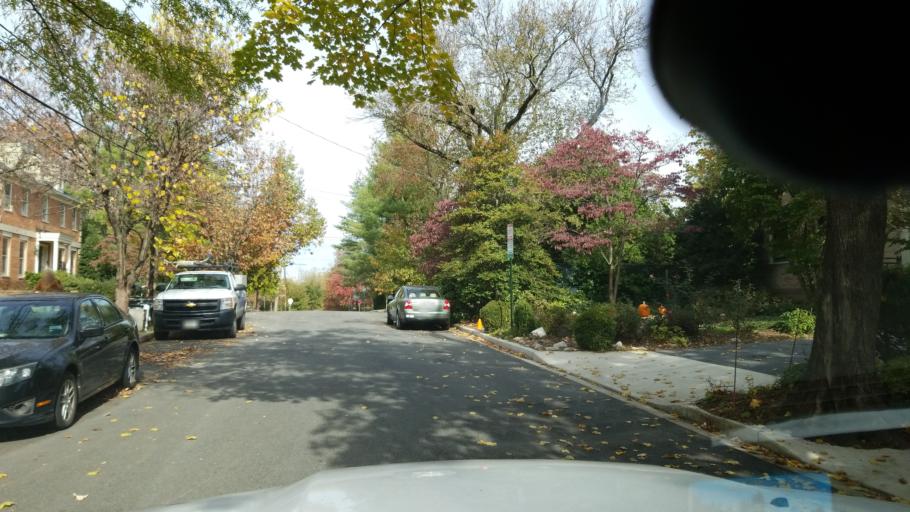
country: US
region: Maryland
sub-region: Montgomery County
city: Chevy Chase Village
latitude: 38.9523
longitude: -77.0652
